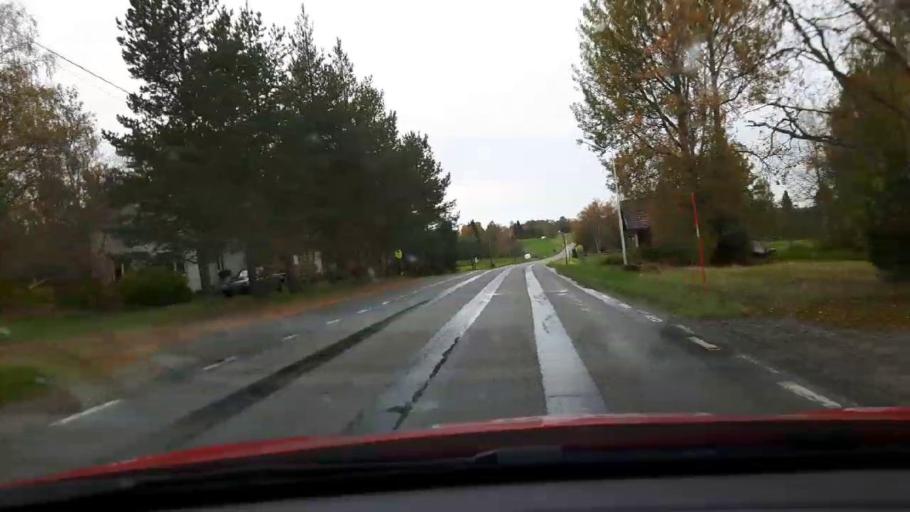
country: SE
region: Jaemtland
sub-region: Bergs Kommun
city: Hoverberg
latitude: 62.8839
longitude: 14.3593
